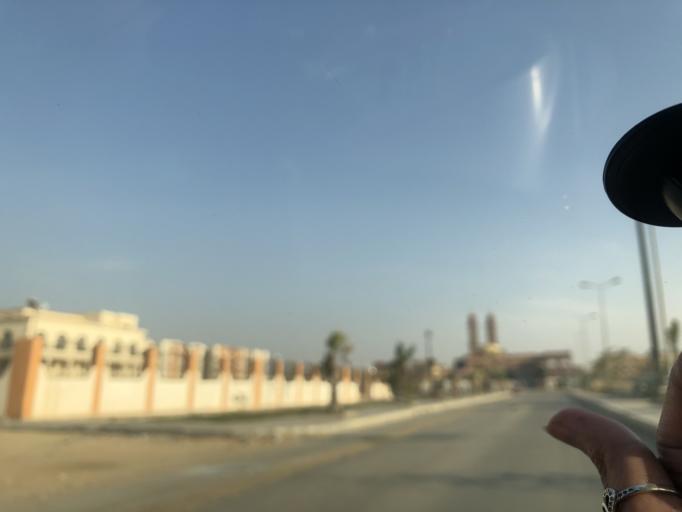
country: EG
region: Al Jizah
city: Madinat Sittah Uktubar
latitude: 29.9060
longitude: 30.9342
